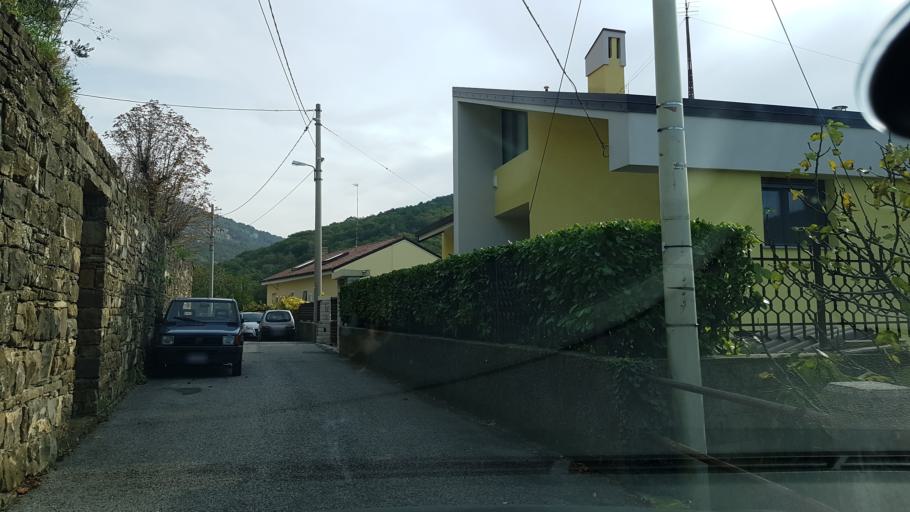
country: IT
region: Friuli Venezia Giulia
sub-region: Provincia di Trieste
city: Trieste
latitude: 45.6494
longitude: 13.8117
